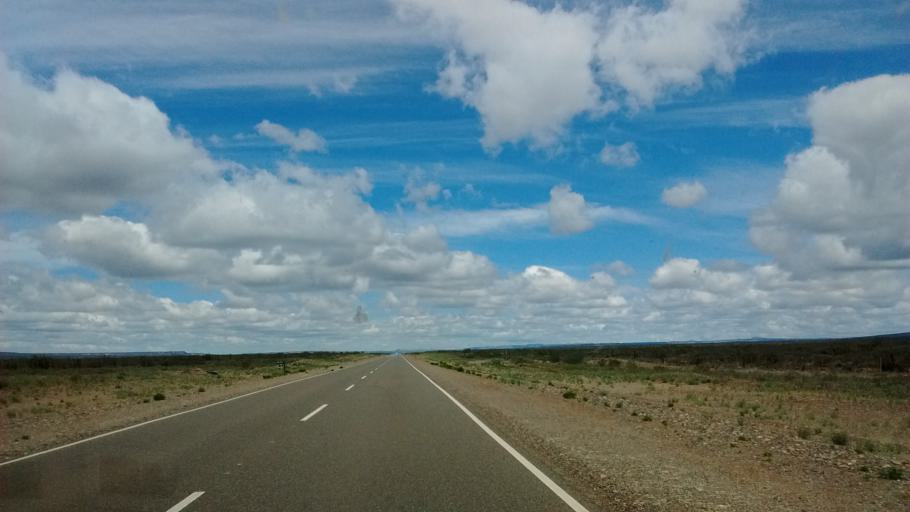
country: AR
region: Neuquen
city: Piedra del Aguila
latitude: -39.8121
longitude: -69.7180
